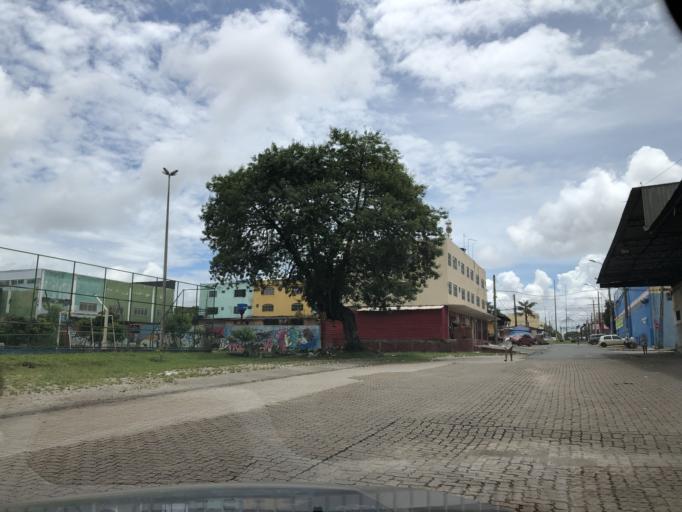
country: BR
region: Federal District
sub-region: Brasilia
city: Brasilia
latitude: -15.8127
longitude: -48.1136
